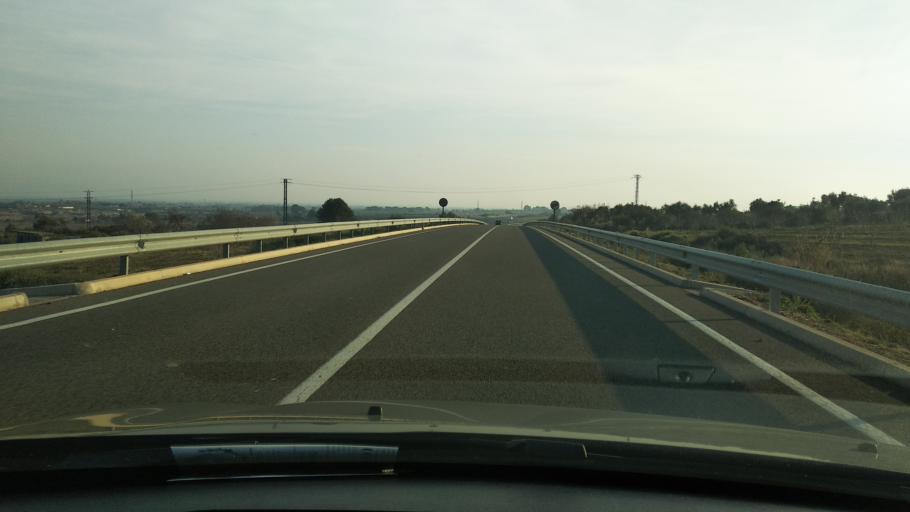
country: ES
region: Catalonia
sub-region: Provincia de Tarragona
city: les Borges del Camp
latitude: 41.1717
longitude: 1.0096
